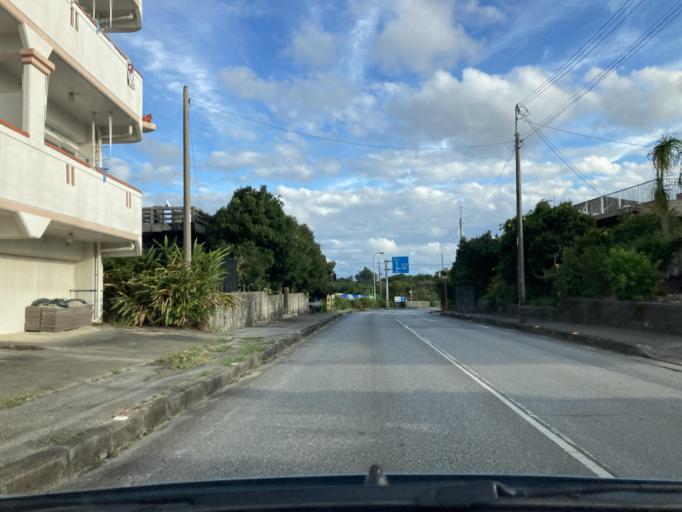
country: JP
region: Okinawa
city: Tomigusuku
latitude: 26.1433
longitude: 127.7469
